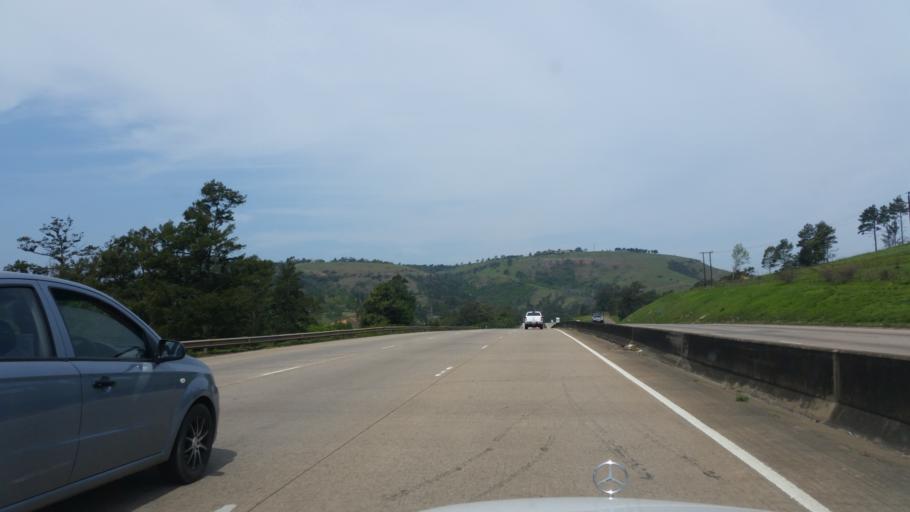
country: ZA
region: KwaZulu-Natal
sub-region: eThekwini Metropolitan Municipality
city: Mpumalanga
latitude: -29.7374
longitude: 30.6505
